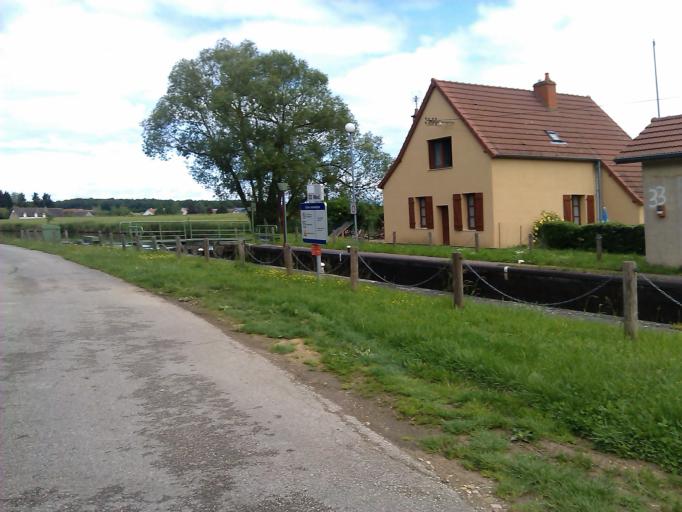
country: FR
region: Bourgogne
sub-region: Departement de Saone-et-Loire
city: Champforgeuil
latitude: 46.8415
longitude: 4.8257
